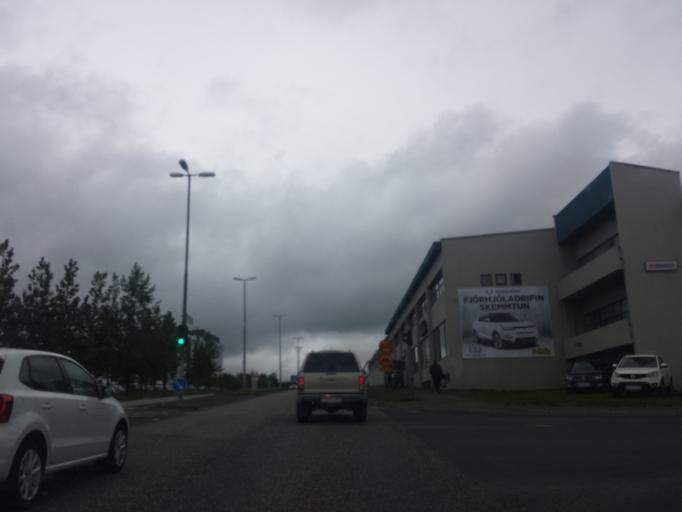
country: IS
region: Capital Region
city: Reykjavik
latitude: 64.1275
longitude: -21.8123
